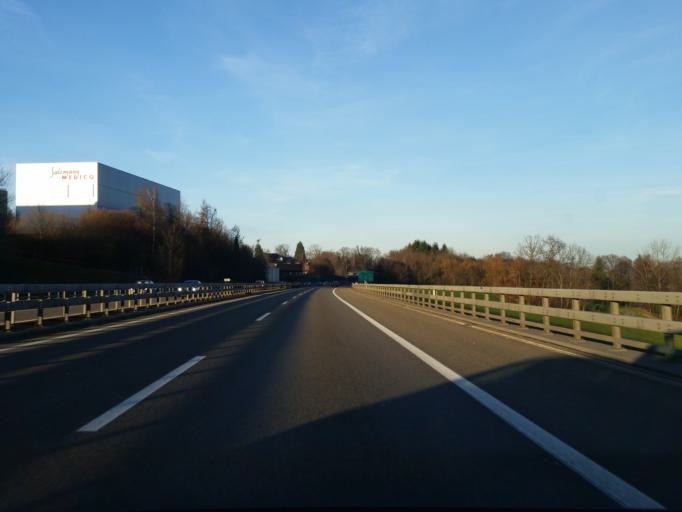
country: CH
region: Saint Gallen
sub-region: Wahlkreis Rorschach
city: Morschwil
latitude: 47.4450
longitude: 9.4190
